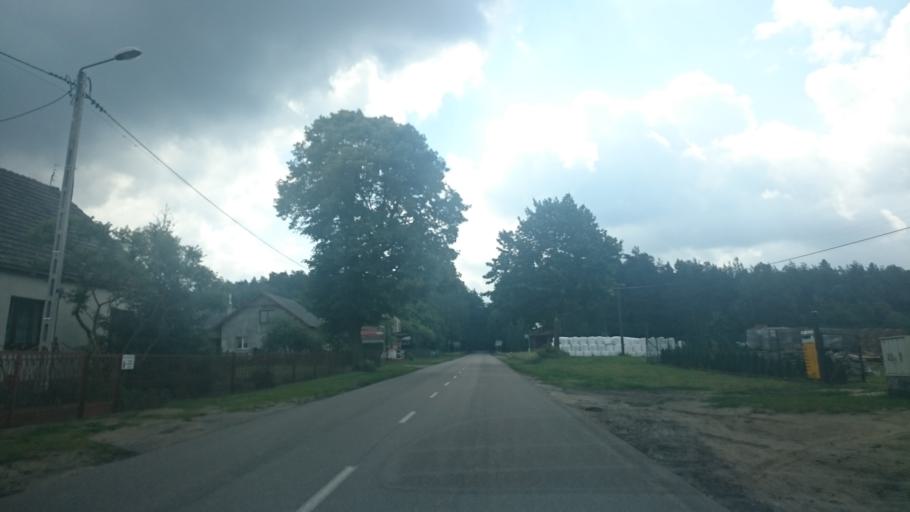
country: PL
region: Pomeranian Voivodeship
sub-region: Powiat koscierski
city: Stara Kiszewa
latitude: 53.9753
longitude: 18.2311
